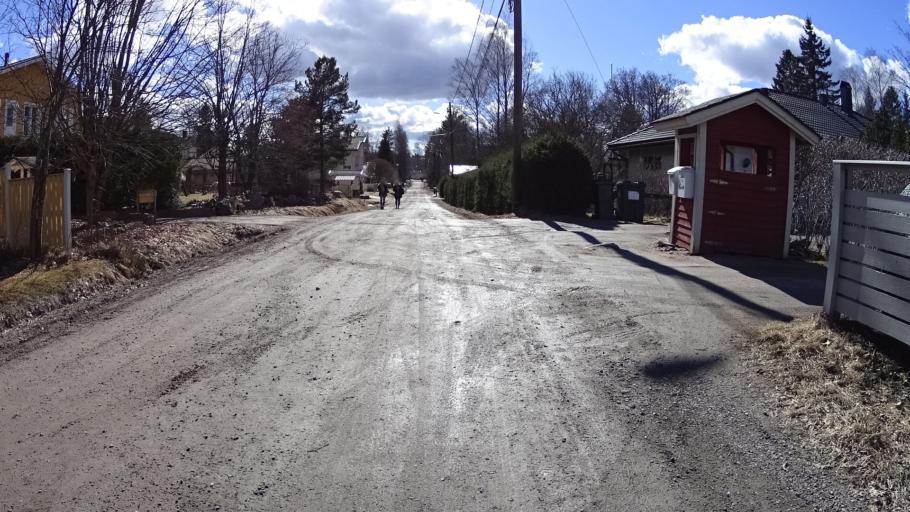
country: FI
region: Uusimaa
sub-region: Helsinki
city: Kauniainen
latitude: 60.2279
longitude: 24.7060
